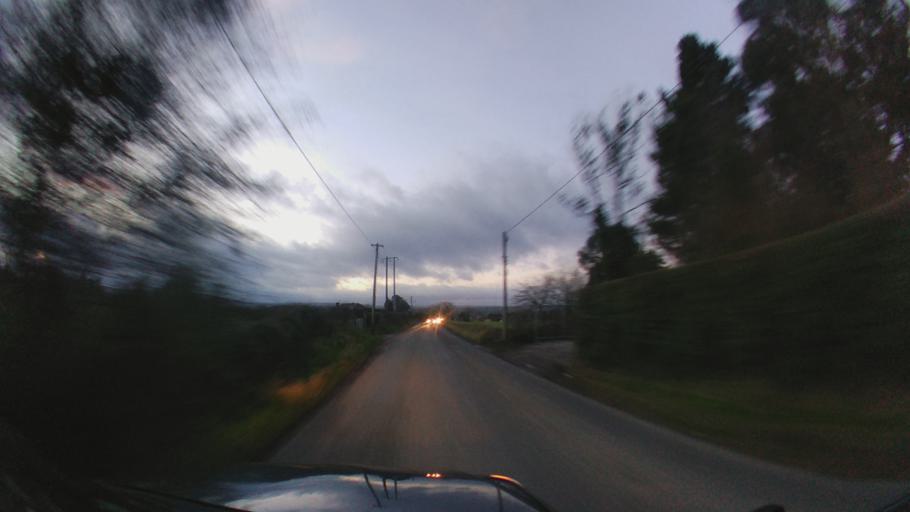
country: IE
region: Leinster
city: Balrothery
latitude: 53.5806
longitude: -6.1750
